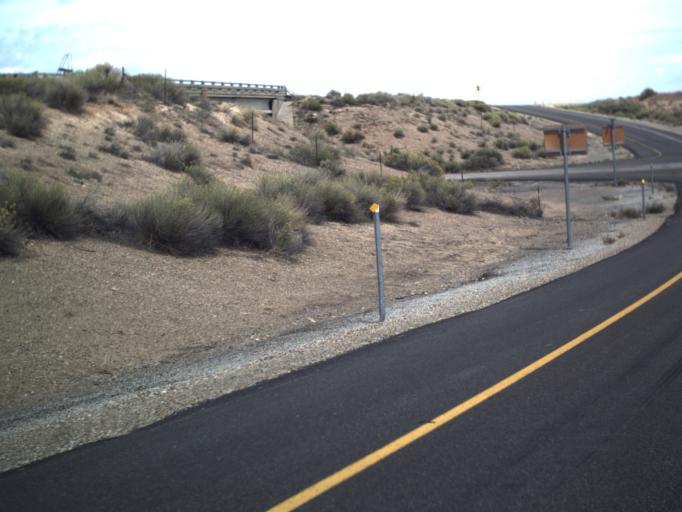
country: US
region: Colorado
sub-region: Mesa County
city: Loma
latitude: 39.0364
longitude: -109.2835
